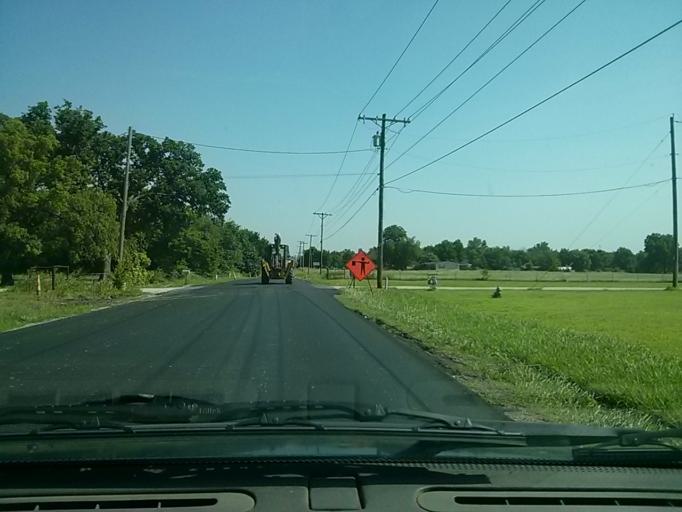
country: US
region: Oklahoma
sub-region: Rogers County
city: Catoosa
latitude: 36.1494
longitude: -95.7617
